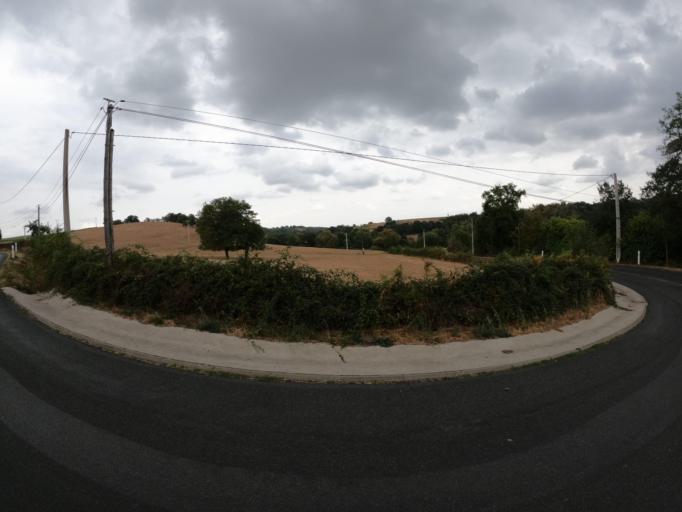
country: FR
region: Pays de la Loire
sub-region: Departement de Maine-et-Loire
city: Le Longeron
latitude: 47.0116
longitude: -1.0749
